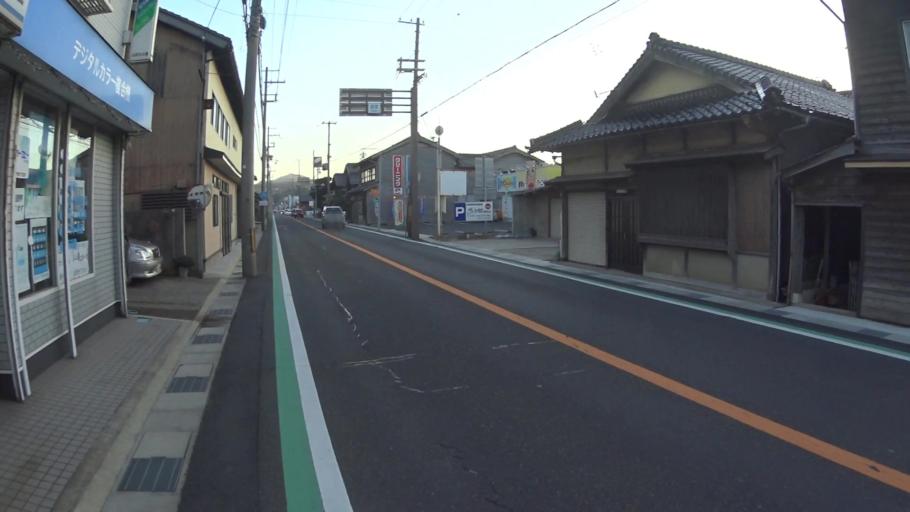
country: JP
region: Kyoto
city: Miyazu
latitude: 35.6779
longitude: 135.0284
